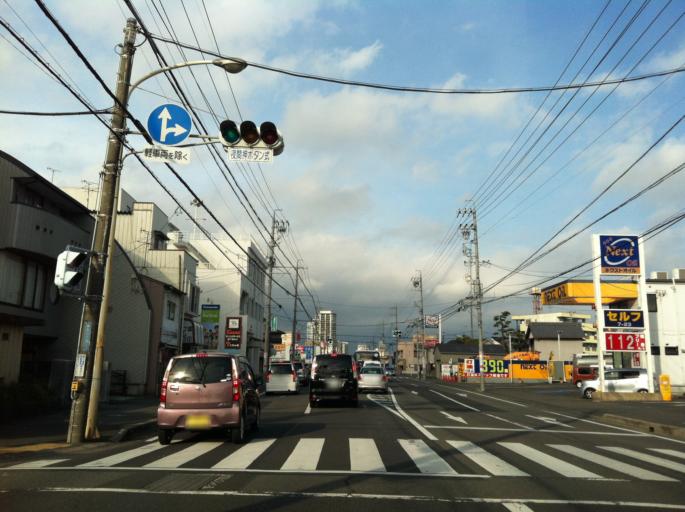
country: JP
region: Shizuoka
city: Shizuoka-shi
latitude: 34.9757
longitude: 138.4052
